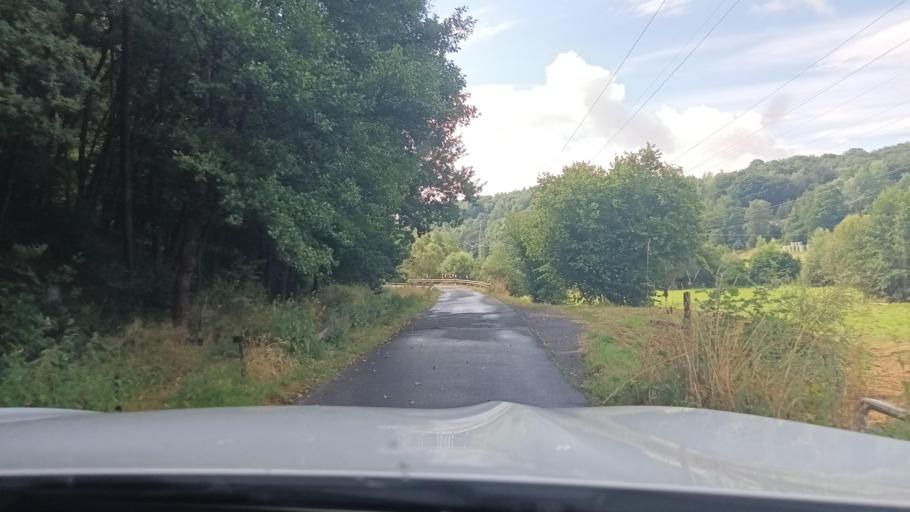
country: DE
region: North Rhine-Westphalia
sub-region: Regierungsbezirk Koln
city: Hennef
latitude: 50.7373
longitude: 7.3161
